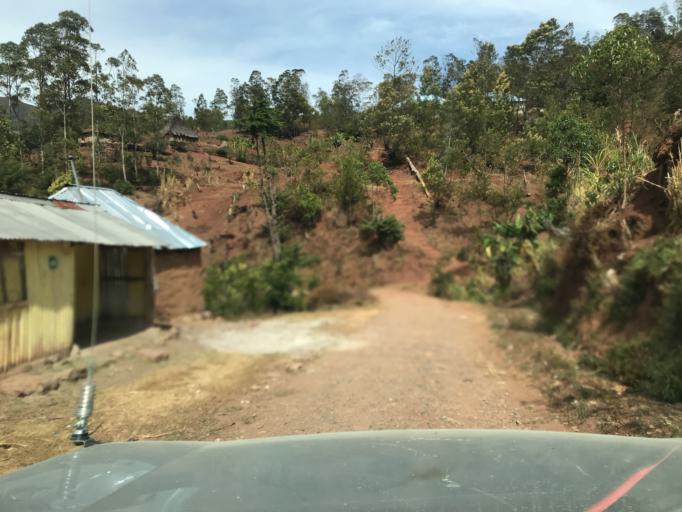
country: TL
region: Ainaro
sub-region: Ainaro
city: Ainaro
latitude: -8.8860
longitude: 125.5213
